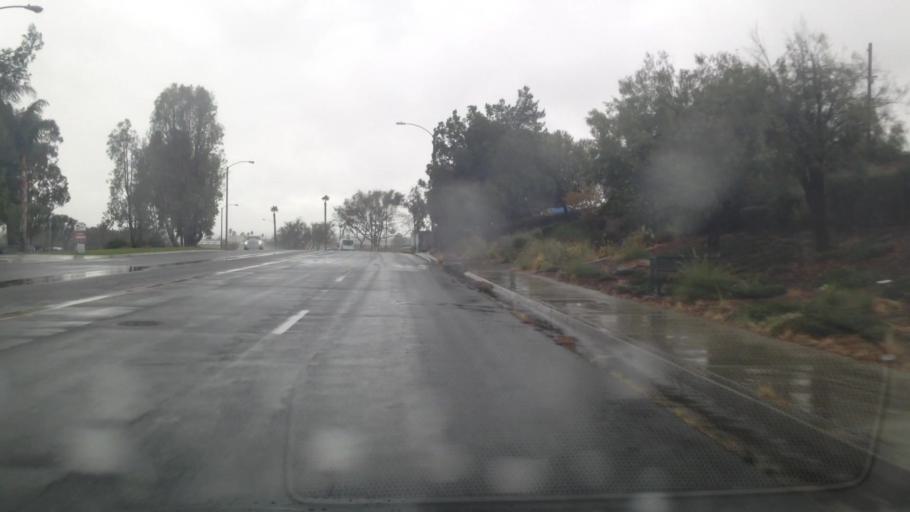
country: US
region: California
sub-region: Riverside County
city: Pedley
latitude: 33.9556
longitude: -117.4438
